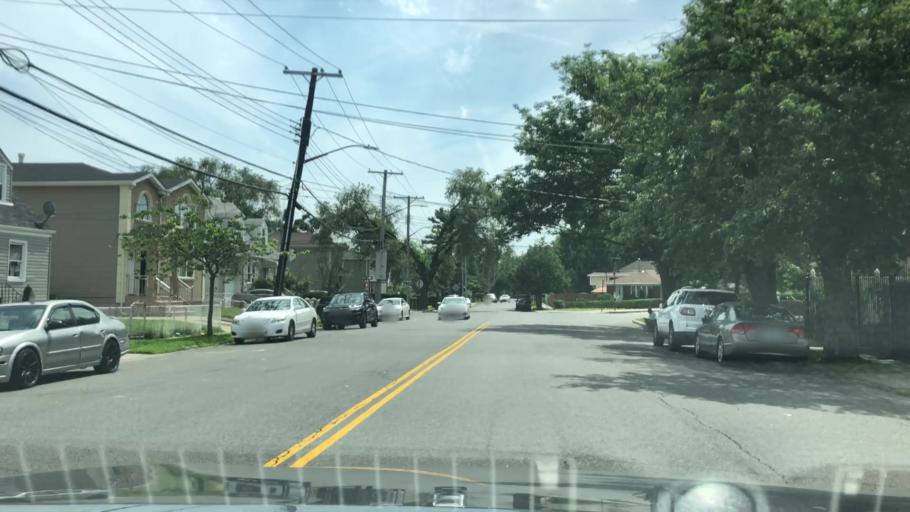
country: US
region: New York
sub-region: Queens County
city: Jamaica
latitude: 40.6972
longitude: -73.7758
